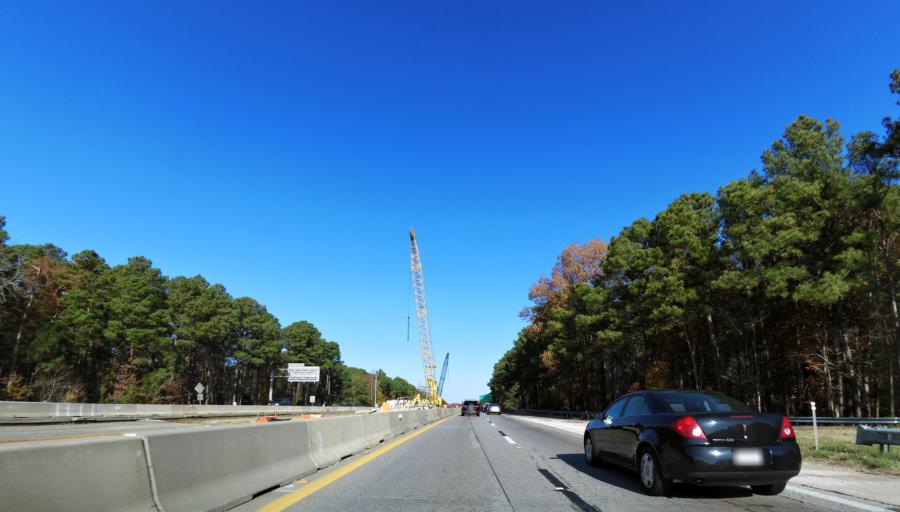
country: US
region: Virginia
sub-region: York County
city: Yorktown
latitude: 37.1733
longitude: -76.5512
